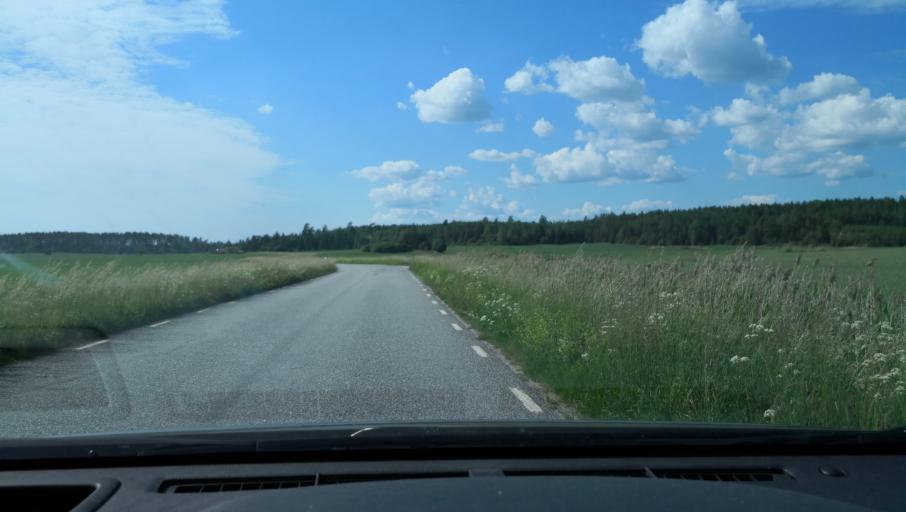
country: SE
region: Uppsala
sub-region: Enkopings Kommun
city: Orsundsbro
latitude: 59.8364
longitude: 17.3030
